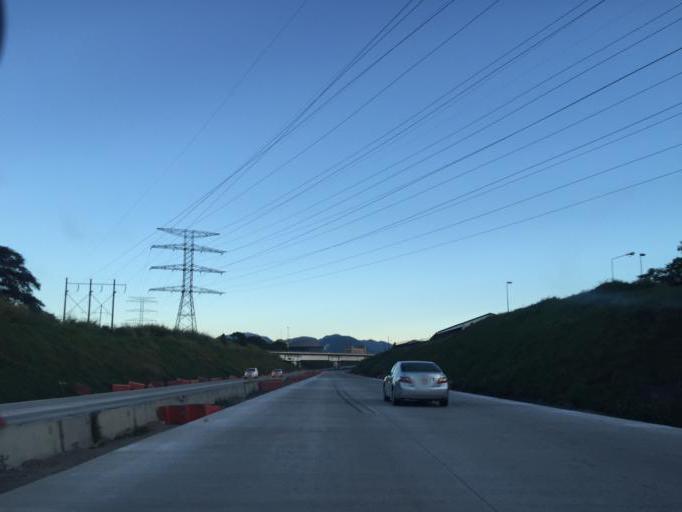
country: MX
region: Veracruz
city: Ixtac Zoquitlan
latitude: 18.8615
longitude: -97.0689
